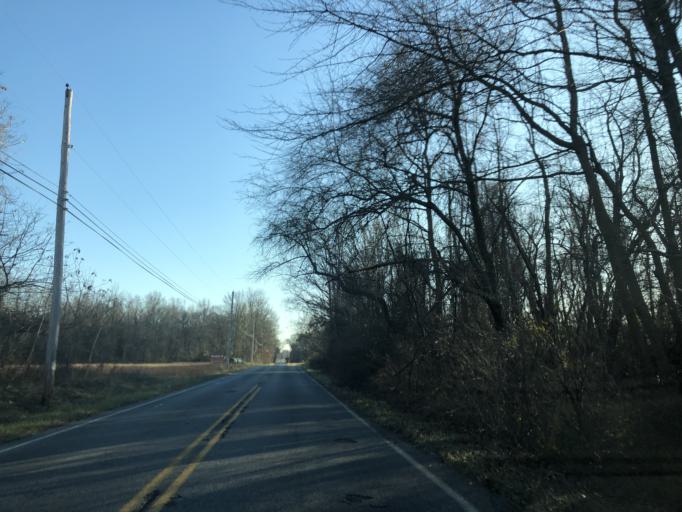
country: US
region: New Jersey
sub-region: Gloucester County
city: Beckett
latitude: 39.7282
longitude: -75.4058
